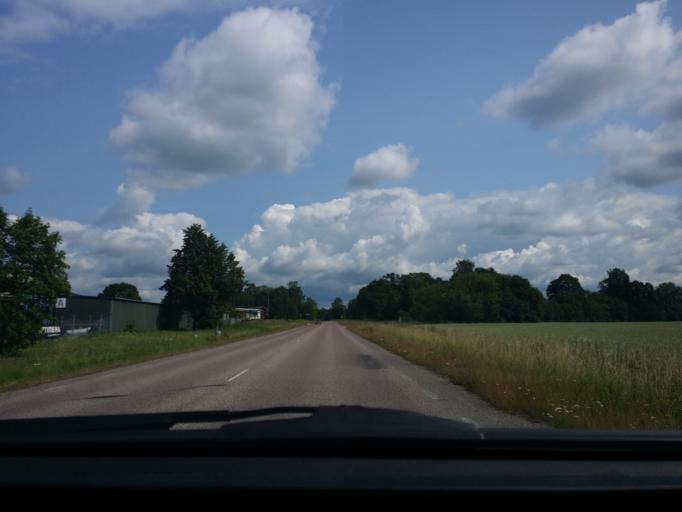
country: SE
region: Vaestmanland
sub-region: Vasteras
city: Hokasen
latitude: 59.6153
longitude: 16.6174
